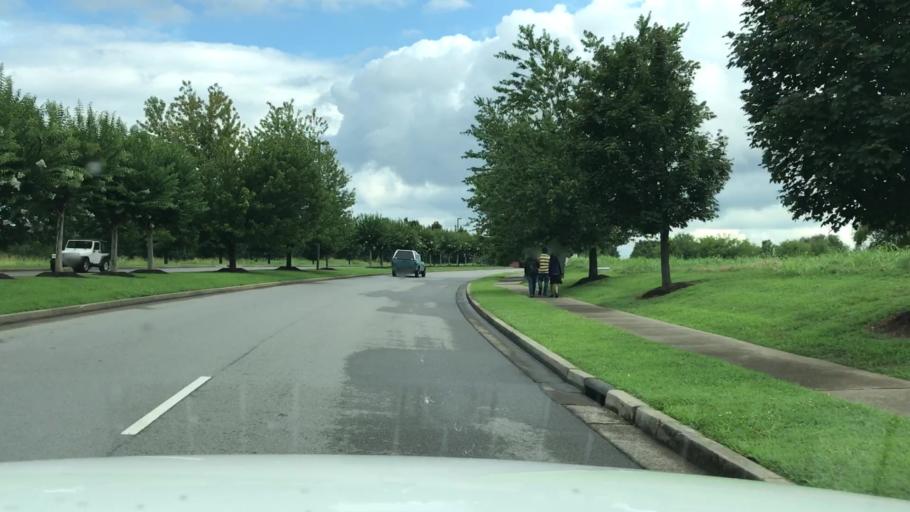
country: US
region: Tennessee
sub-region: Sumner County
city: Hendersonville
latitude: 36.3184
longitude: -86.5956
